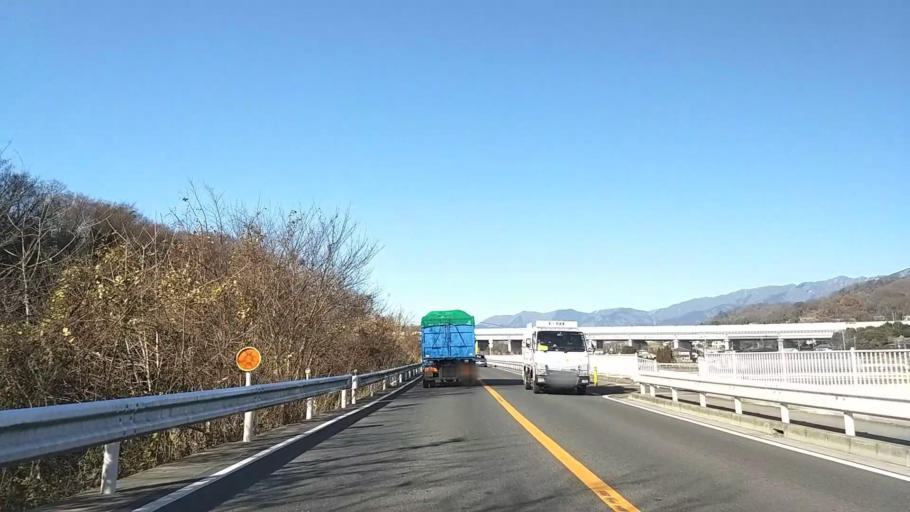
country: JP
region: Kanagawa
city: Hadano
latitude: 35.3573
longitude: 139.2558
